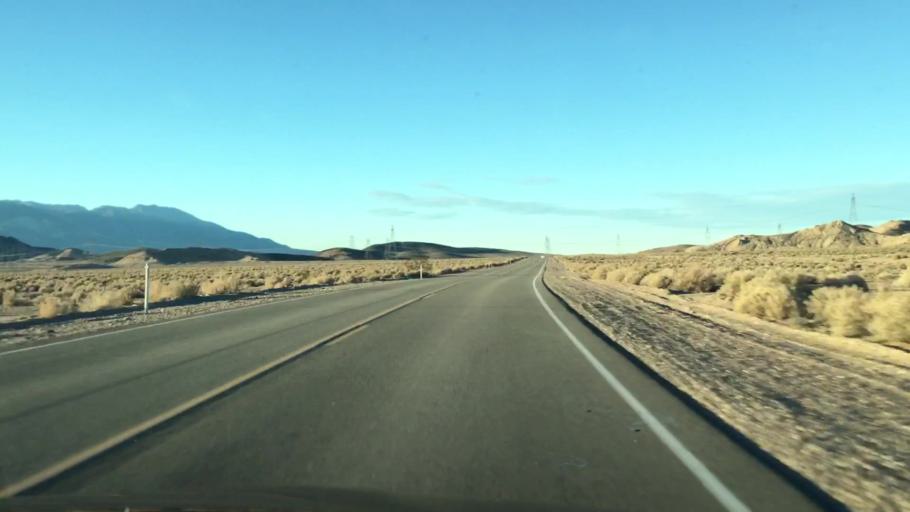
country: US
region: California
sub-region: San Bernardino County
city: Fort Irwin
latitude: 35.3760
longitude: -116.1213
